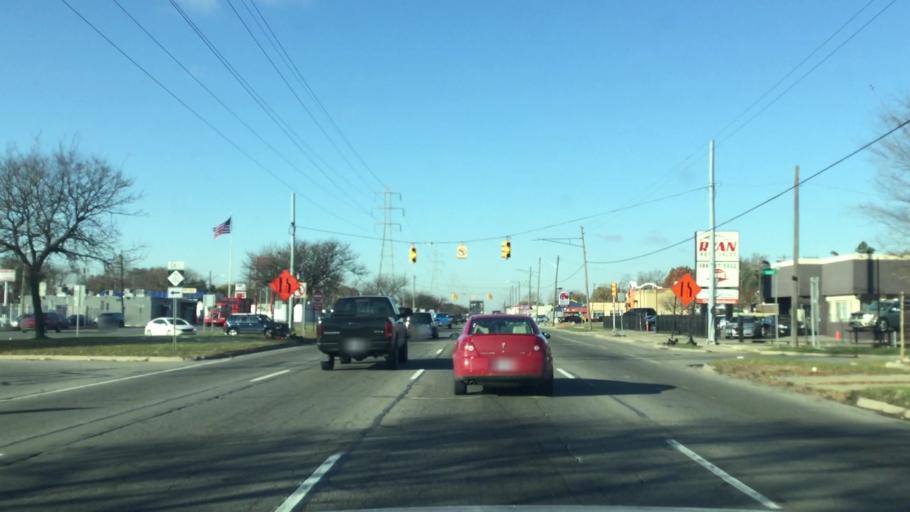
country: US
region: Michigan
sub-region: Macomb County
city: Warren
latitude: 42.4476
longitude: -83.0613
